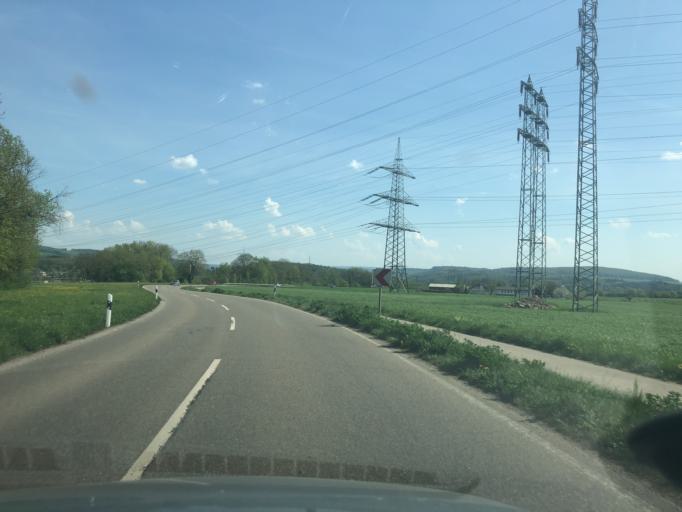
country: CH
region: Aargau
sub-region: Bezirk Zurzach
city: Koblenz
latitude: 47.6360
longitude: 8.2494
